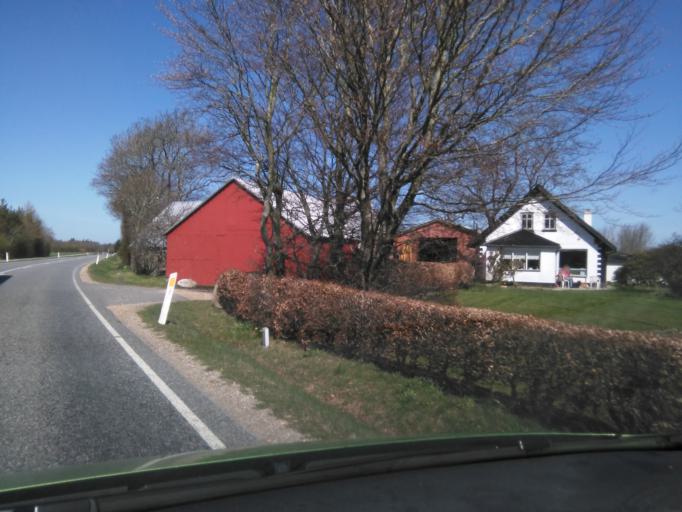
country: DK
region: South Denmark
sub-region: Varde Kommune
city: Olgod
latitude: 55.7138
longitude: 8.7409
